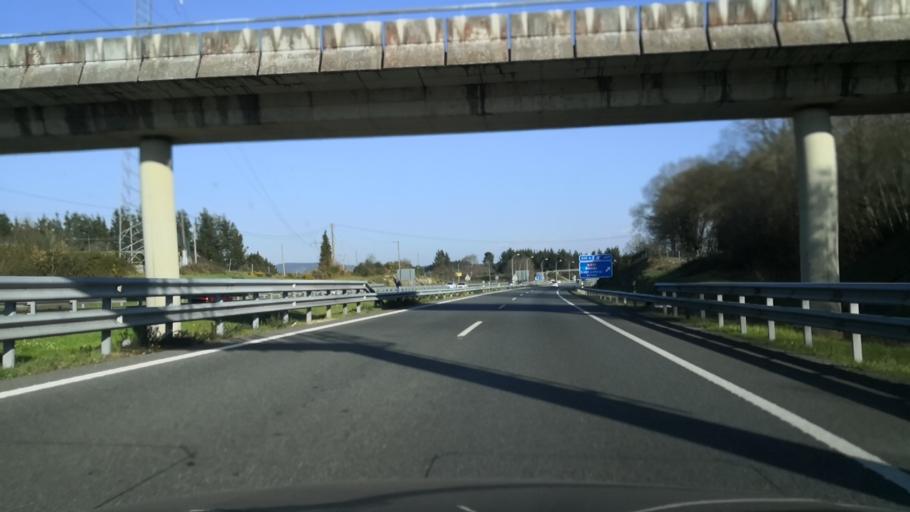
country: ES
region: Galicia
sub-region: Provincia de Lugo
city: Lugo
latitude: 43.0470
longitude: -7.5344
